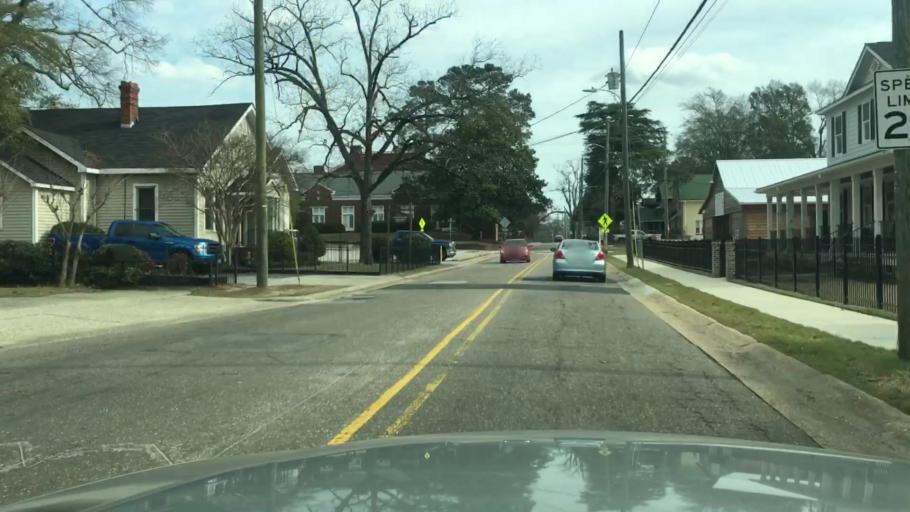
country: US
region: North Carolina
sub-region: Cumberland County
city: Fayetteville
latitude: 35.0550
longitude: -78.9001
